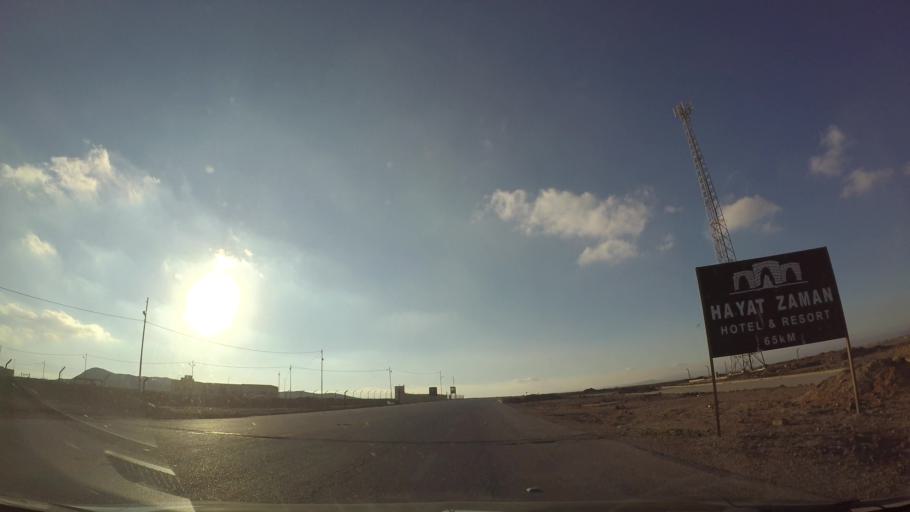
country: JO
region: Tafielah
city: Busayra
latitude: 30.4991
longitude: 35.7959
